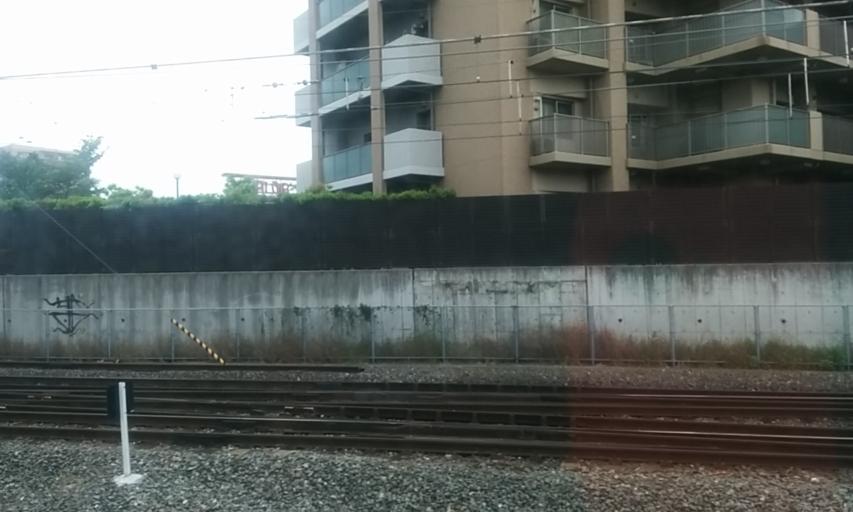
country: JP
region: Osaka
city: Moriguchi
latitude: 34.6878
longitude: 135.5649
